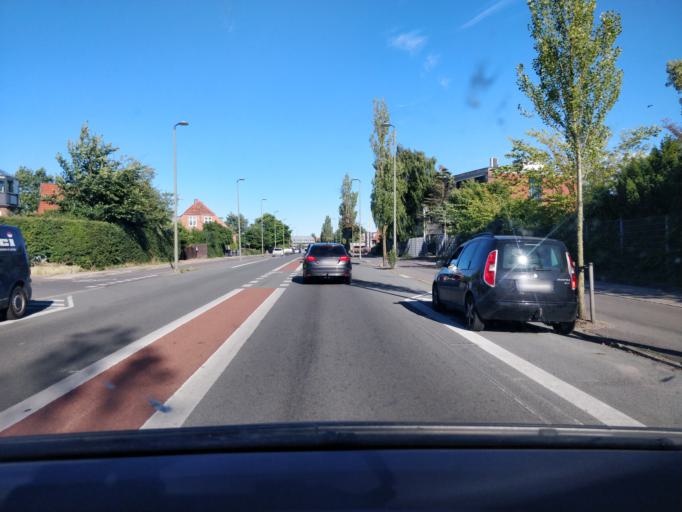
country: DK
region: Capital Region
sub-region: Kobenhavn
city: Vanlose
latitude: 55.6988
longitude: 12.4729
